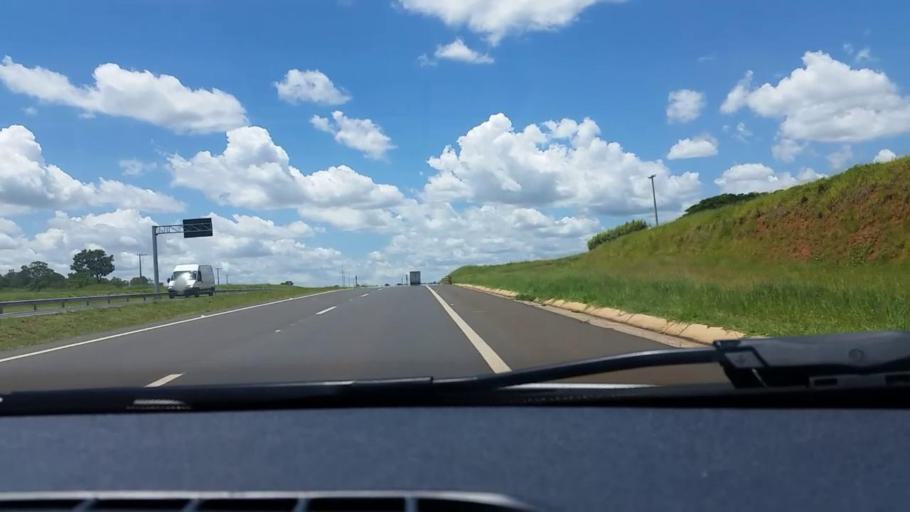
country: BR
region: Sao Paulo
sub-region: Bauru
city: Bauru
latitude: -22.4430
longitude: -49.1520
